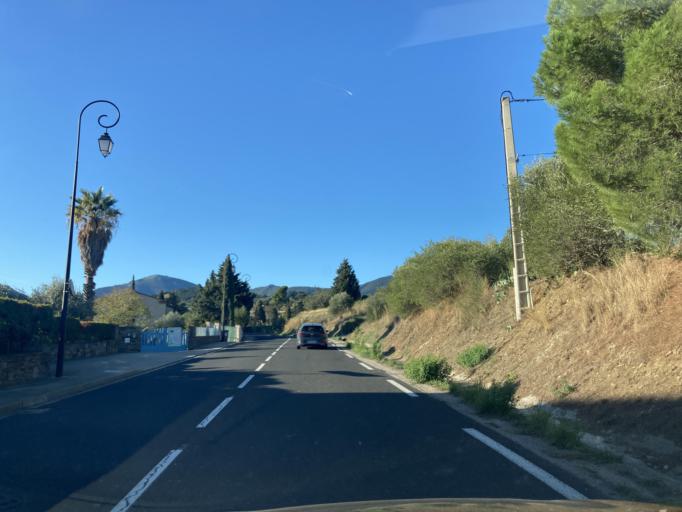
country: FR
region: Languedoc-Roussillon
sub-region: Departement des Pyrenees-Orientales
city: Collioure
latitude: 42.5285
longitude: 3.0756
